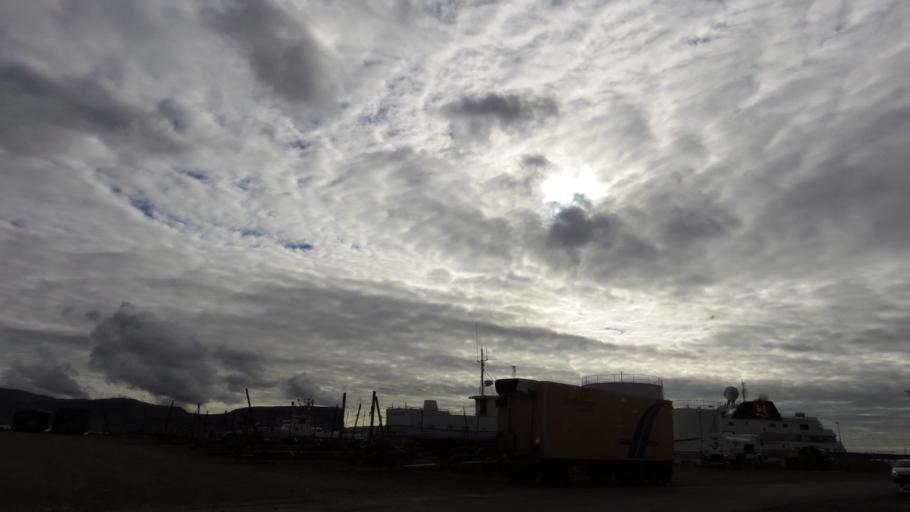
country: IS
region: West
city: Olafsvik
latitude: 65.5952
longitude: -24.0024
